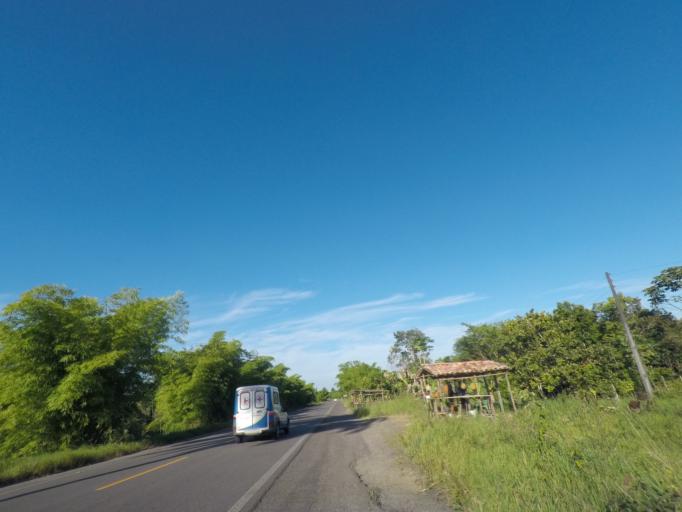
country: BR
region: Bahia
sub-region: Nazare
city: Nazare
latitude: -13.0067
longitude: -38.9678
